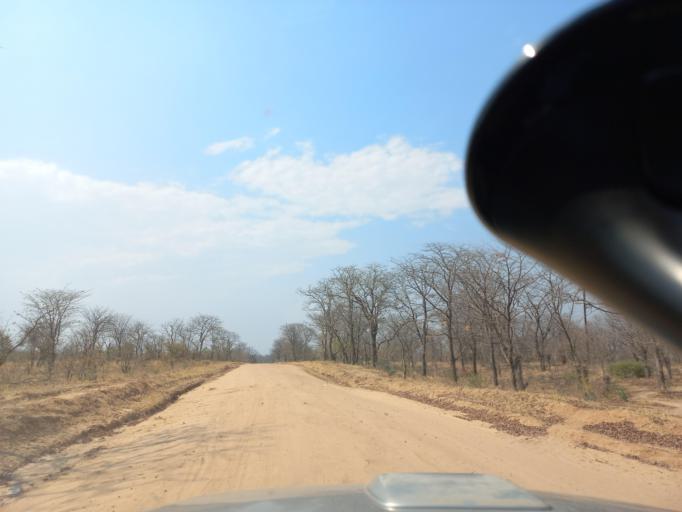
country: ZW
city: Chirundu
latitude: -15.9369
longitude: 28.9145
